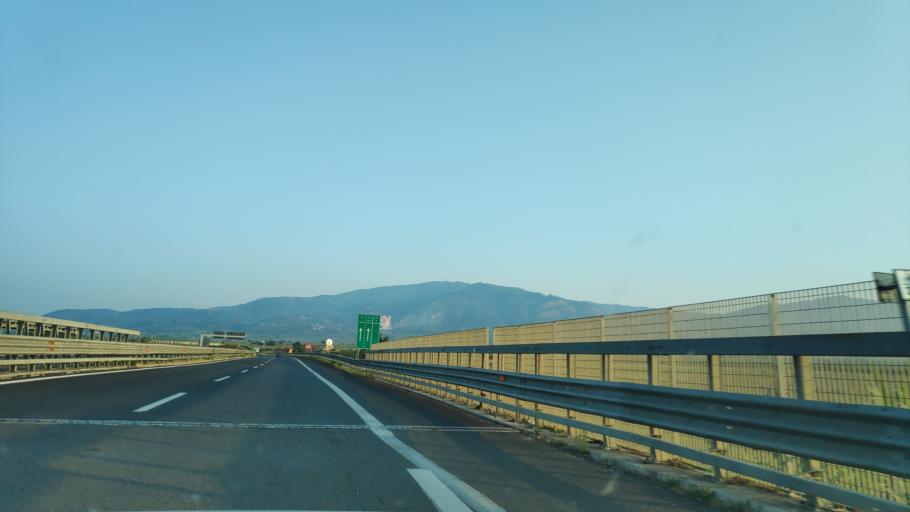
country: IT
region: Calabria
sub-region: Provincia di Catanzaro
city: Santa Eufemia Lamezia
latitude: 38.9197
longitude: 16.2638
